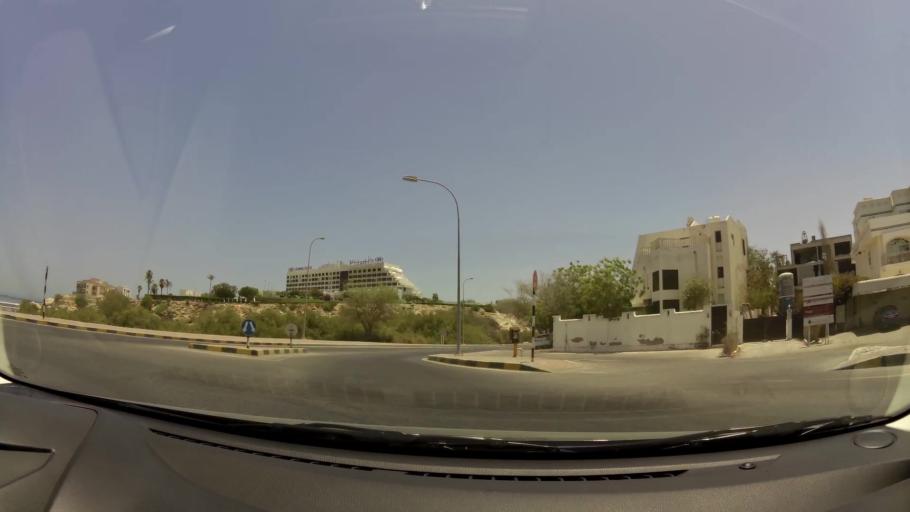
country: OM
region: Muhafazat Masqat
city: Bawshar
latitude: 23.6260
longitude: 58.4828
